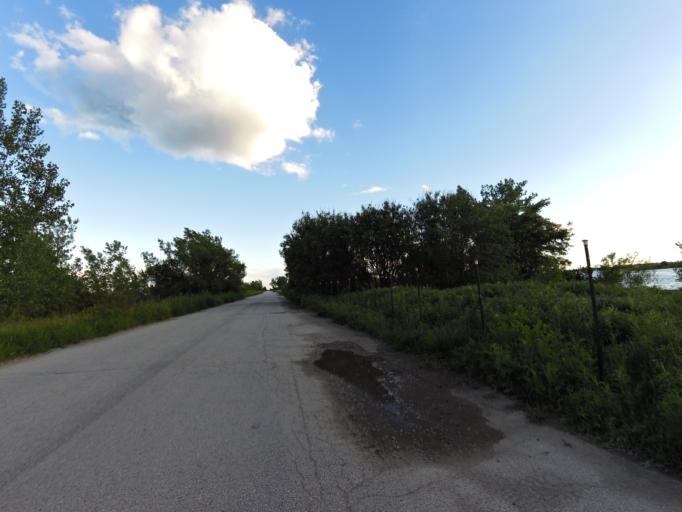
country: CA
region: Ontario
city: Toronto
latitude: 43.6394
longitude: -79.3224
